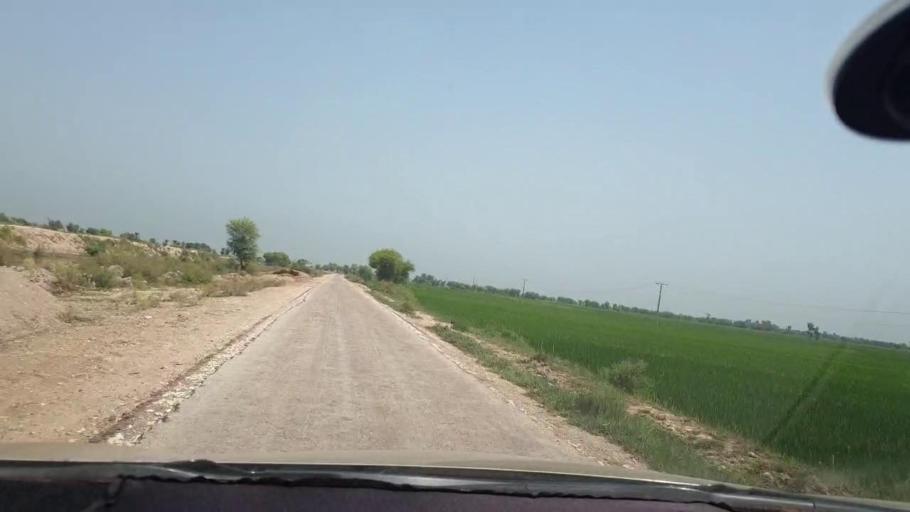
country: PK
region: Sindh
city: Kambar
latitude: 27.6852
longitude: 67.9475
